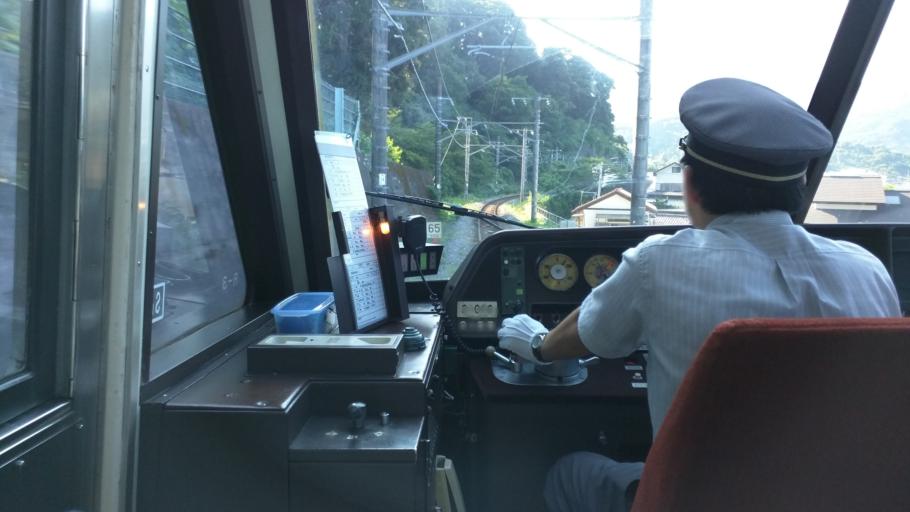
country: JP
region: Shizuoka
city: Ito
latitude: 34.9997
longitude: 139.0829
